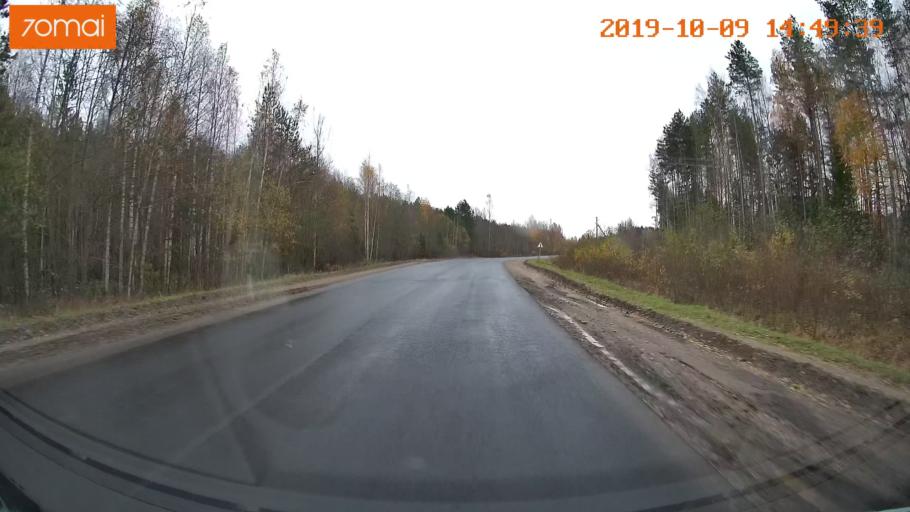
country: RU
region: Kostroma
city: Chistyye Bory
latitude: 58.3913
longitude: 41.5854
